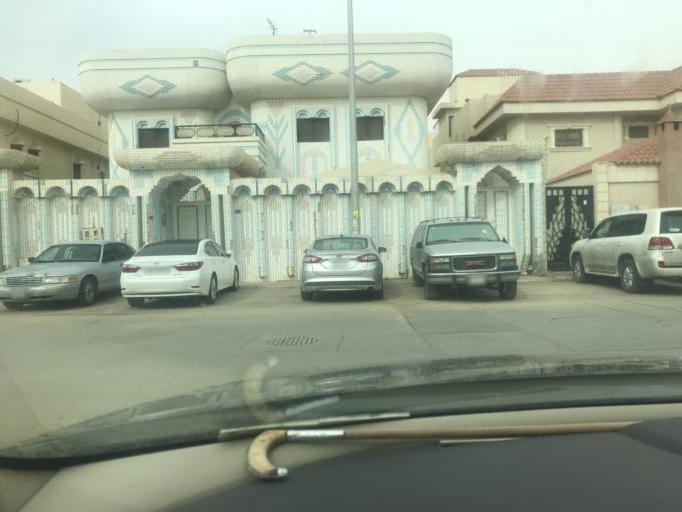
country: SA
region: Ar Riyad
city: Riyadh
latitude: 24.7529
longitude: 46.7640
